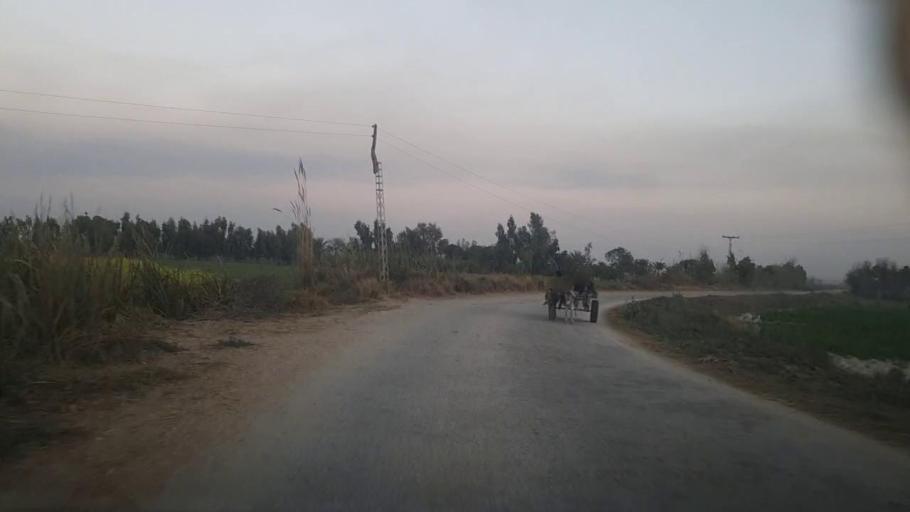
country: PK
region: Sindh
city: Kandiari
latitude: 26.6814
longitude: 68.9423
